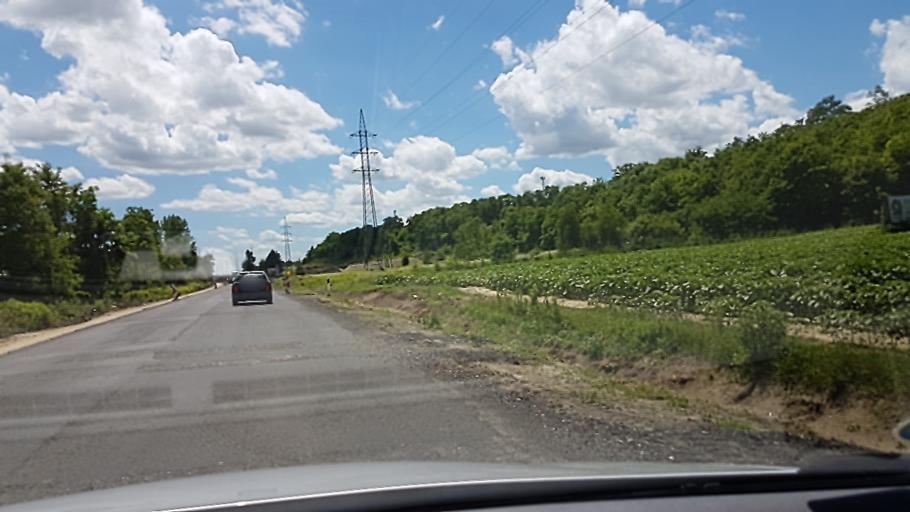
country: HU
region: Zala
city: Zalaegerszeg
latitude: 46.8235
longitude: 16.8625
